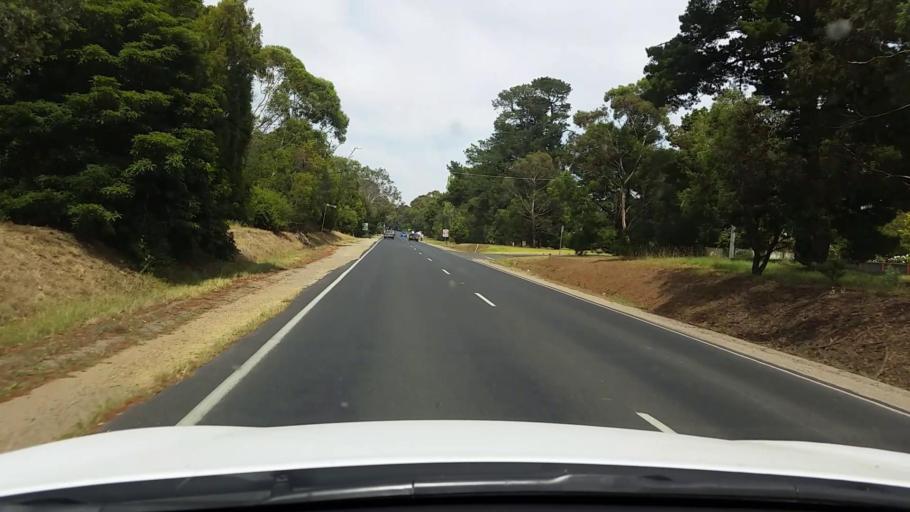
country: AU
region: Victoria
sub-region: Mornington Peninsula
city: Balnarring
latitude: -38.3709
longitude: 145.1312
